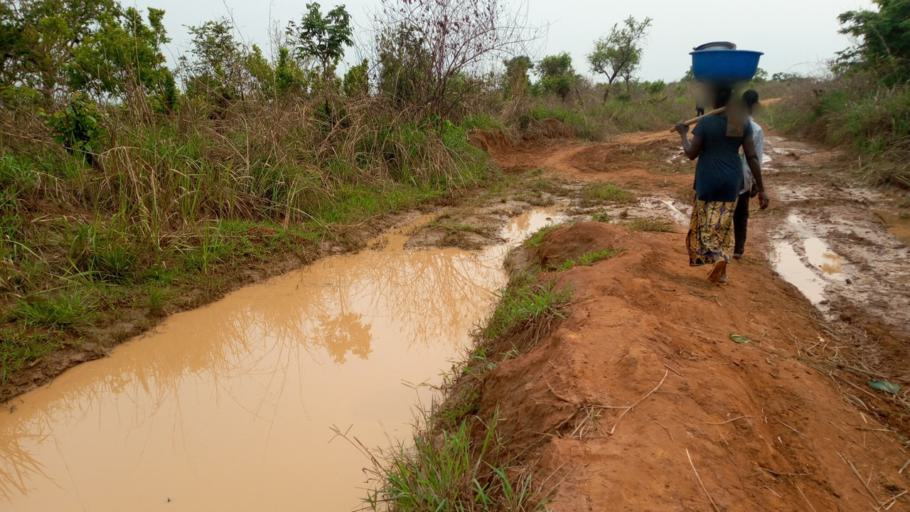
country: CD
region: Bandundu
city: Bandundu
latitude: -3.4636
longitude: 17.7166
